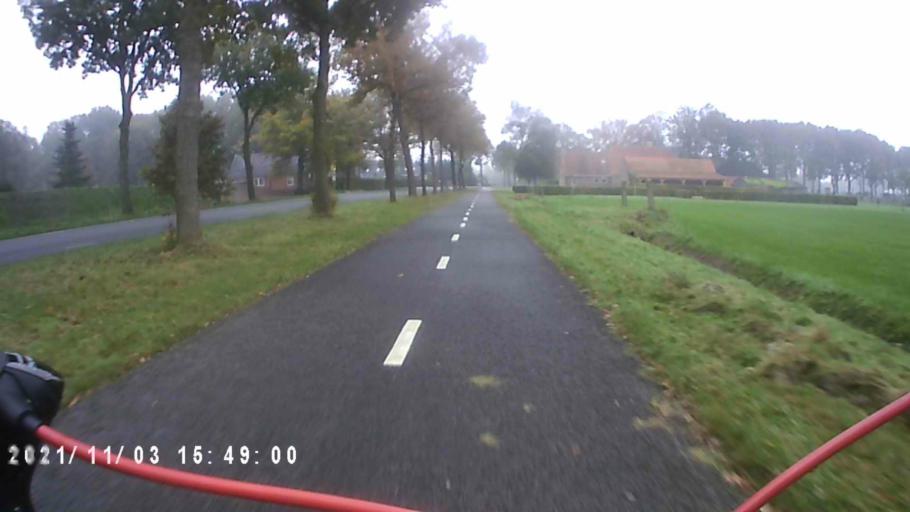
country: NL
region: Groningen
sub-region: Gemeente Leek
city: Leek
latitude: 53.0855
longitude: 6.3386
